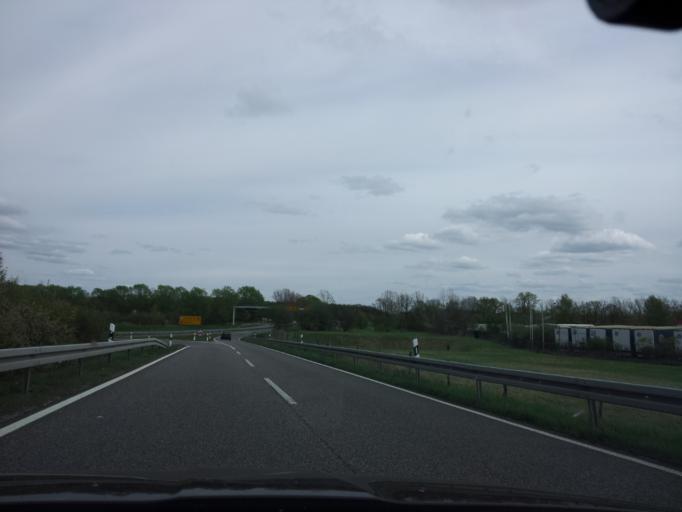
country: DE
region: Brandenburg
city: Grossbeeren
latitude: 52.3807
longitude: 13.3214
